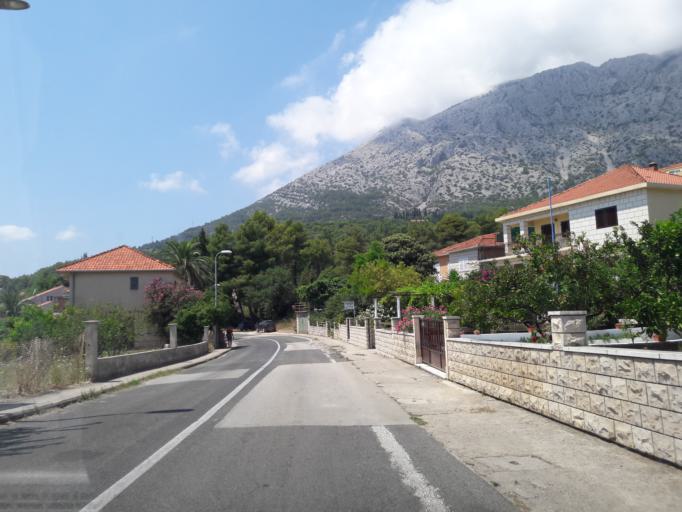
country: HR
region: Dubrovacko-Neretvanska
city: Orebic
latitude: 42.9763
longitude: 17.1730
